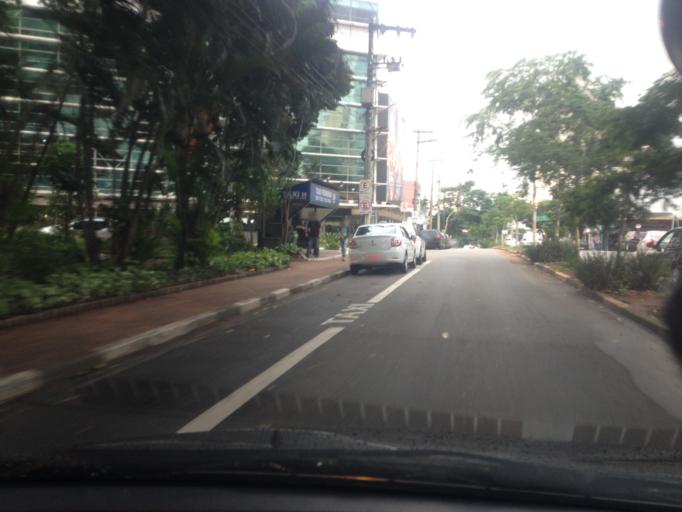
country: BR
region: Sao Paulo
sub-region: Sao Paulo
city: Sao Paulo
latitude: -23.5623
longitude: -46.6924
